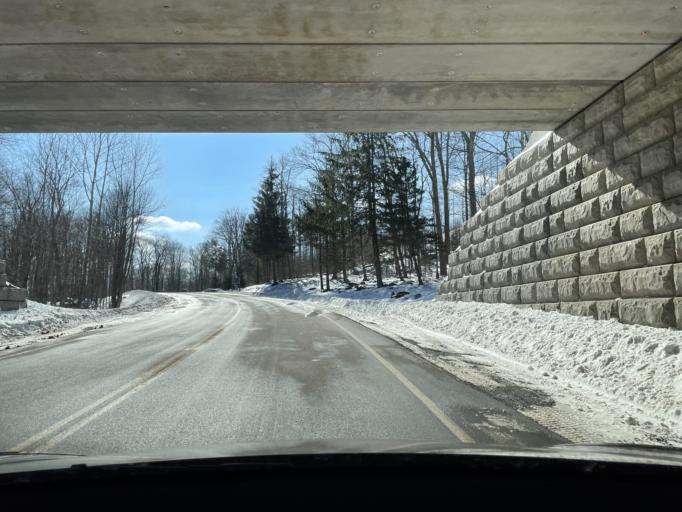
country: US
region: New York
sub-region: Delaware County
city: Stamford
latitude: 42.1376
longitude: -74.5104
